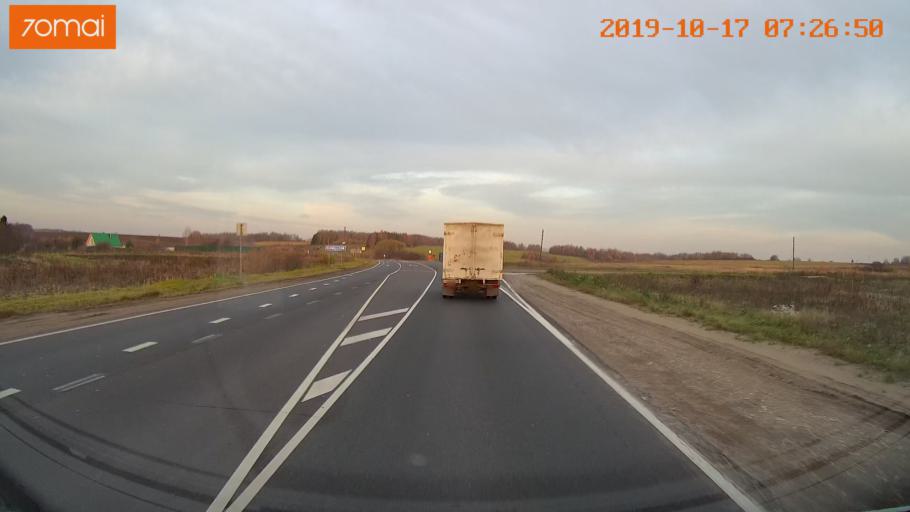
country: RU
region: Ivanovo
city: Gavrilov Posad
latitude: 56.3598
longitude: 40.0882
